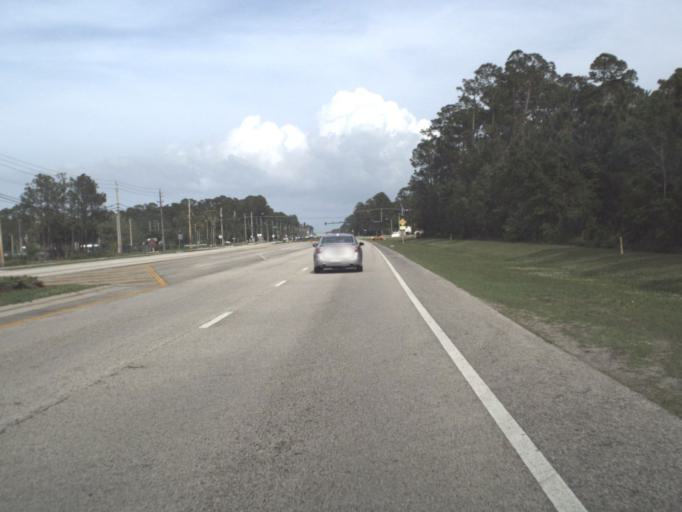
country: US
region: Florida
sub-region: Flagler County
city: Bunnell
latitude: 29.4753
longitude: -81.2116
